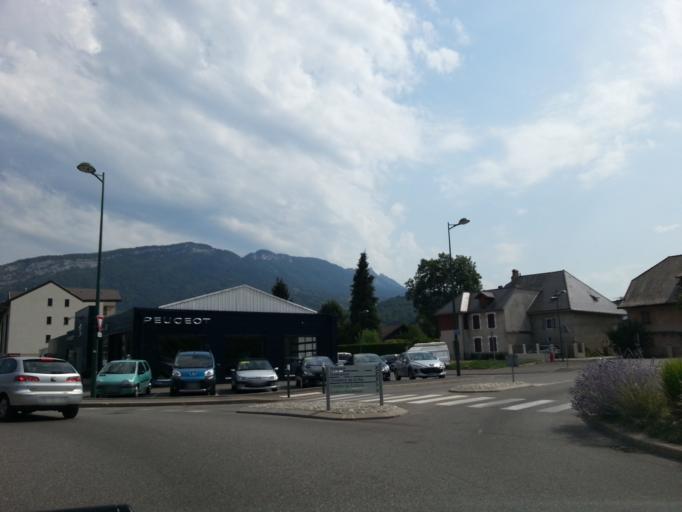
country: FR
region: Rhone-Alpes
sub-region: Departement de la Haute-Savoie
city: Saint-Jorioz
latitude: 45.8360
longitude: 6.1604
